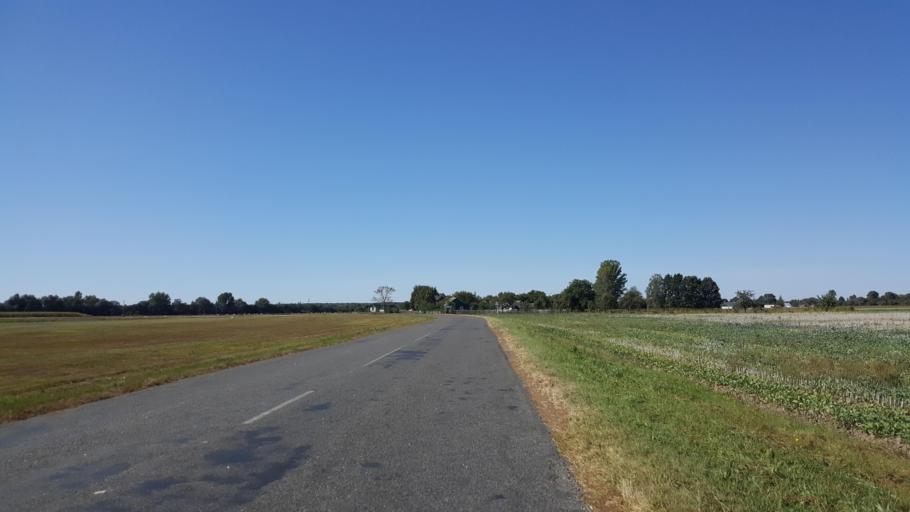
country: BY
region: Brest
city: Charnawchytsy
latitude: 52.2605
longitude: 23.5483
